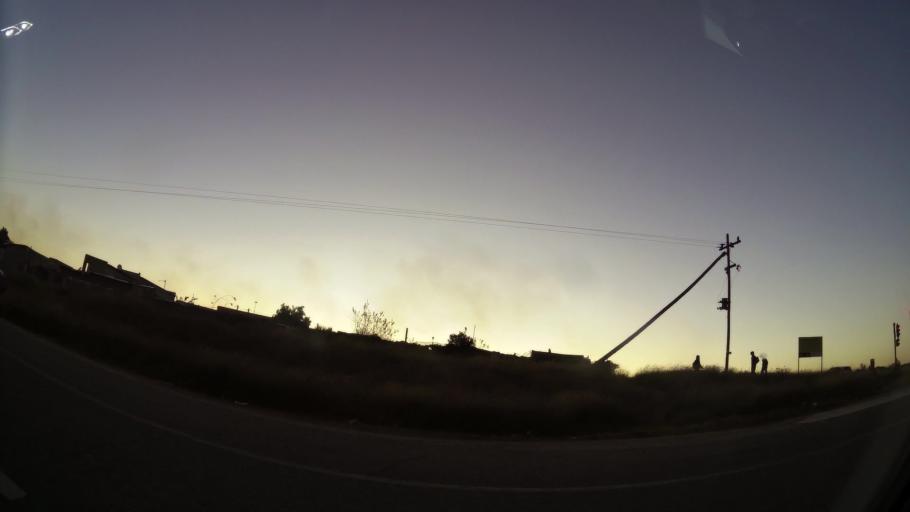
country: ZA
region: Gauteng
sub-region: City of Johannesburg Metropolitan Municipality
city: Diepsloot
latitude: -25.9179
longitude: 28.0241
